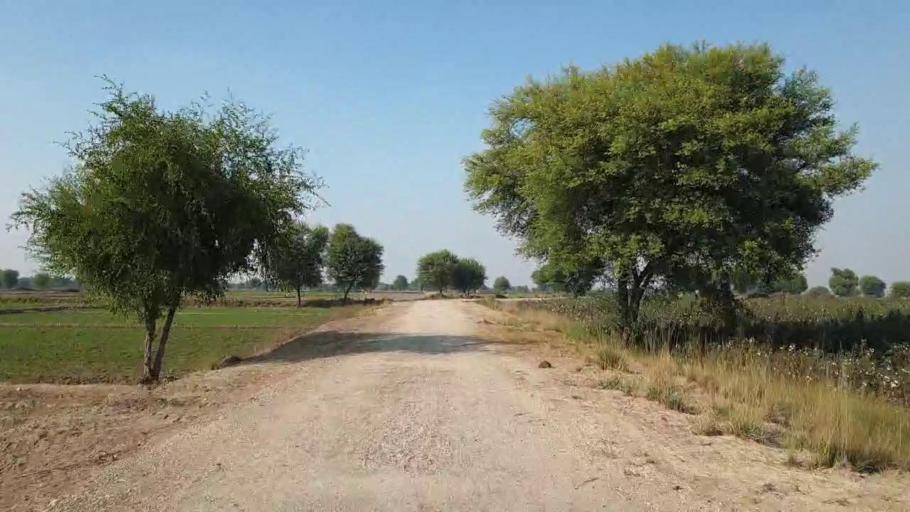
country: PK
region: Sindh
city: Sehwan
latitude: 26.4582
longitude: 67.8156
